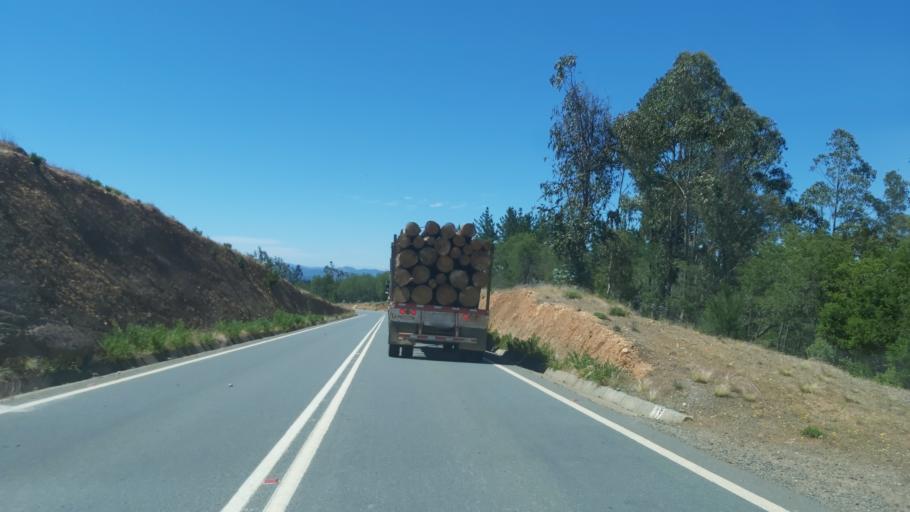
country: CL
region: Maule
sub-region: Provincia de Talca
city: Talca
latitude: -34.9438
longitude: -71.9770
